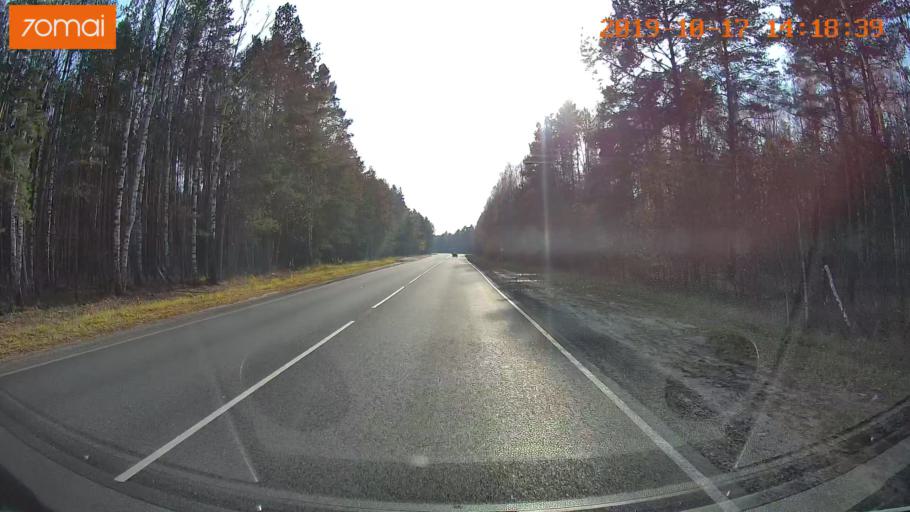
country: RU
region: Rjazan
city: Spas-Klepiki
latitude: 55.0604
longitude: 40.0278
